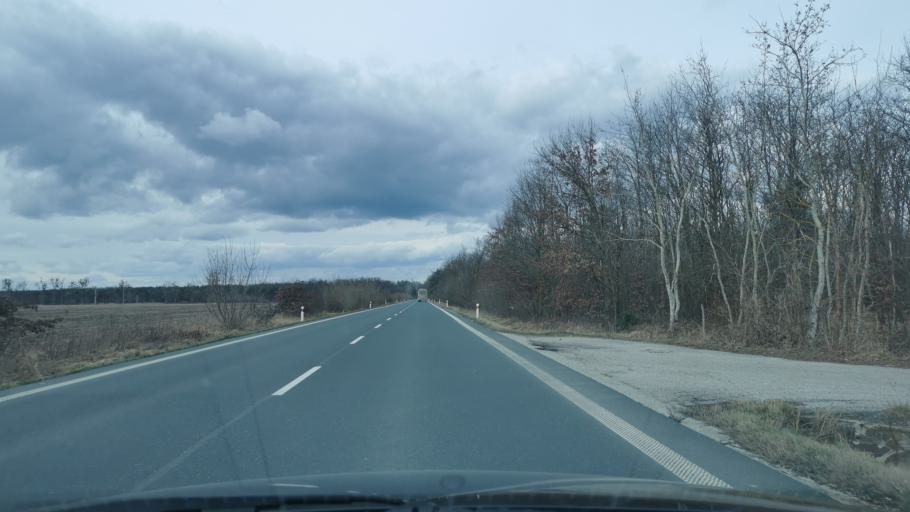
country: CZ
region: South Moravian
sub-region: Okres Breclav
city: Lanzhot
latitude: 48.6938
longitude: 17.0370
